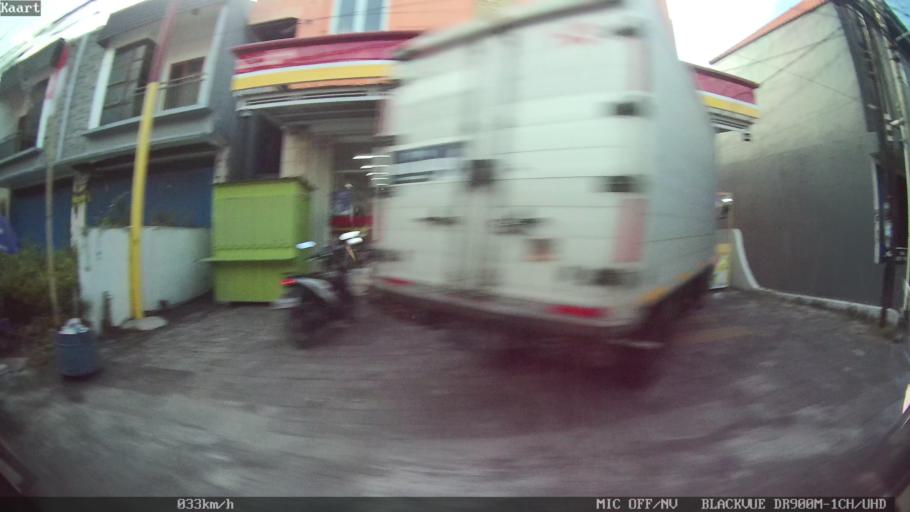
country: ID
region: Bali
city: Karyadharma
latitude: -8.7002
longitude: 115.1916
